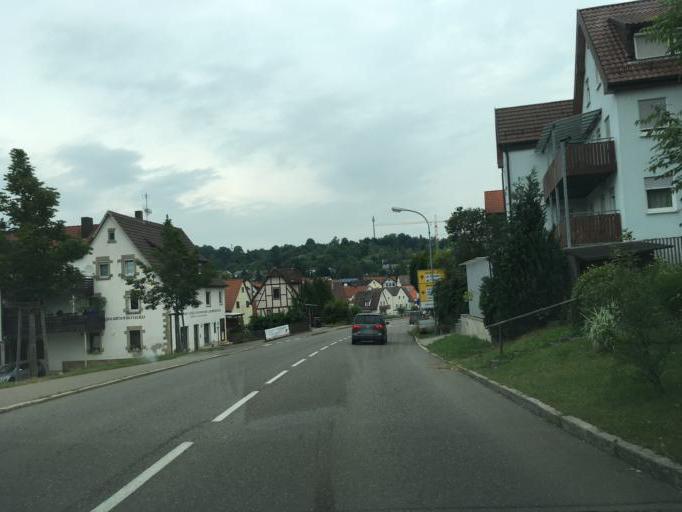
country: DE
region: Baden-Wuerttemberg
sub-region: Tuebingen Region
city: Dettenhausen
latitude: 48.6065
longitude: 9.0989
